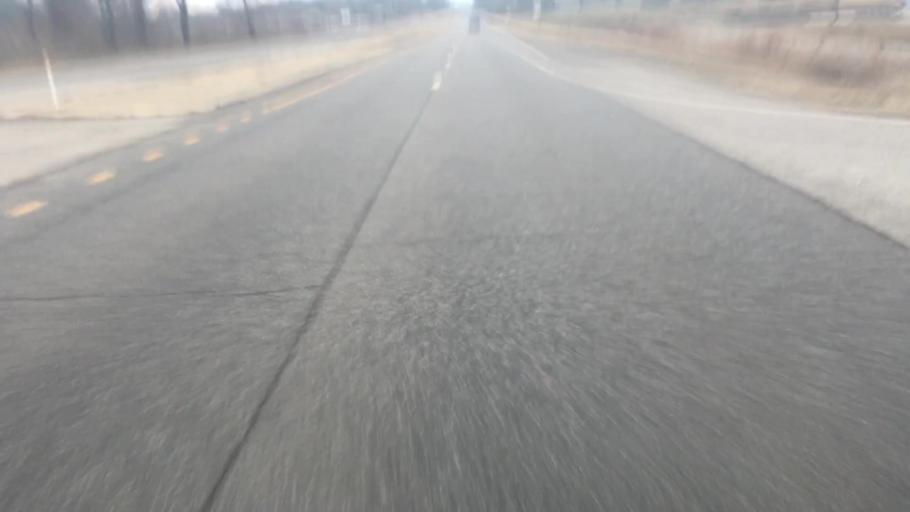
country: US
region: Alabama
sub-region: Walker County
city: Jasper
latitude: 33.8315
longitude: -87.2125
